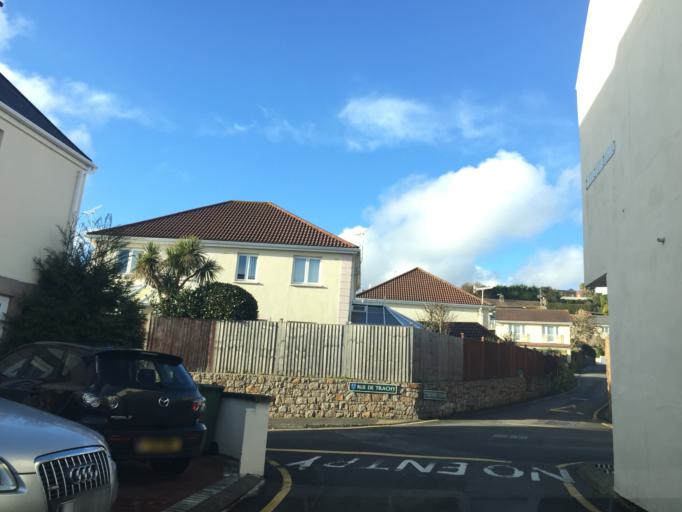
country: JE
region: St Helier
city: Saint Helier
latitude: 49.1983
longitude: -2.1324
